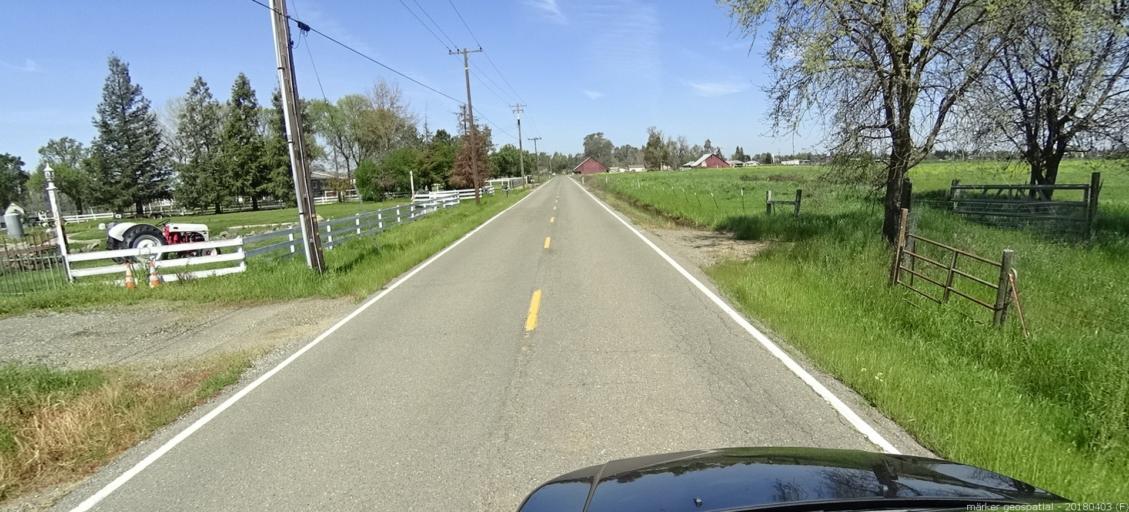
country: US
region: California
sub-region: Sacramento County
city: Wilton
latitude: 38.3961
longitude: -121.2607
